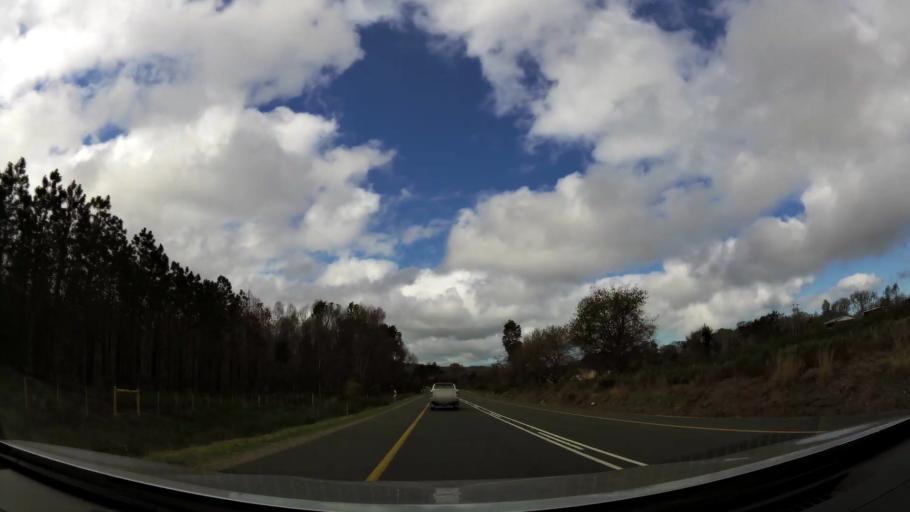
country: ZA
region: Western Cape
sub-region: Eden District Municipality
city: Knysna
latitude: -34.0371
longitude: 23.1342
